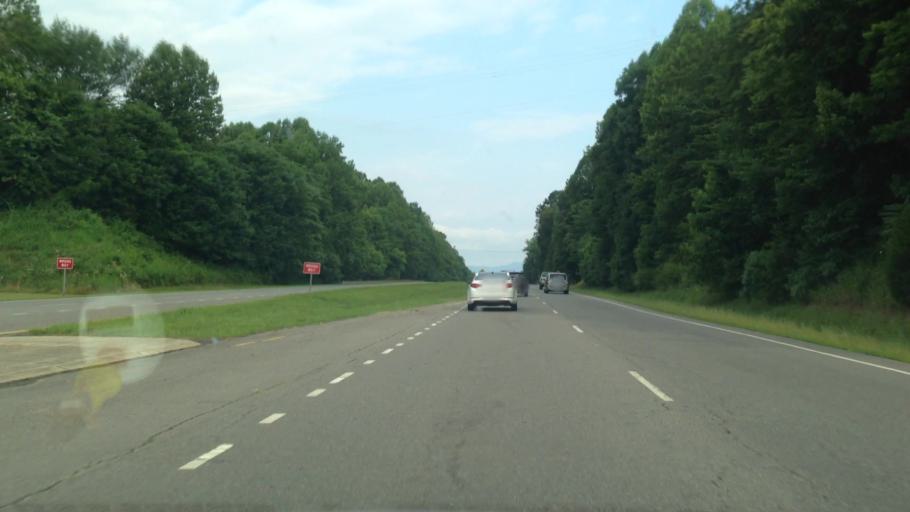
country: US
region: North Carolina
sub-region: Surry County
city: Mount Airy
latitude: 36.4734
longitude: -80.5794
